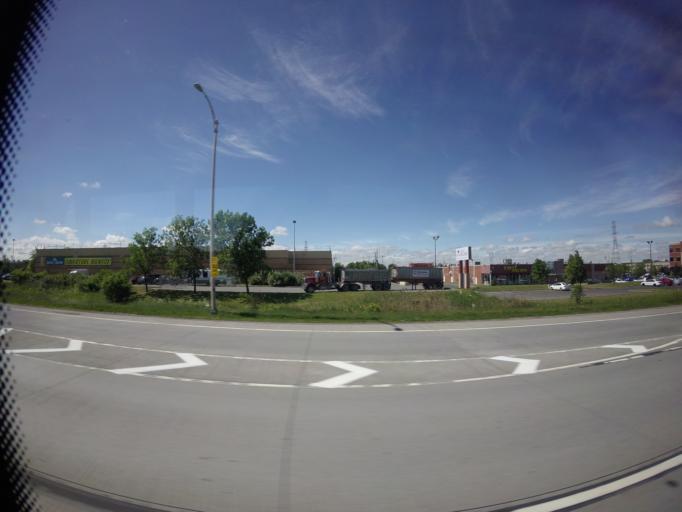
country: CA
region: Quebec
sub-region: Monteregie
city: Boucherville
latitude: 45.5714
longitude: -73.4432
